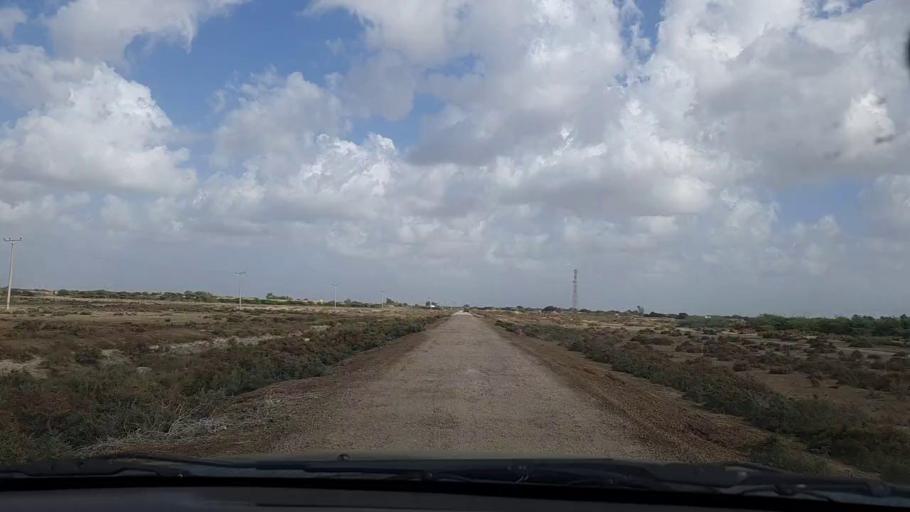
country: PK
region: Sindh
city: Keti Bandar
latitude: 24.1040
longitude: 67.5927
